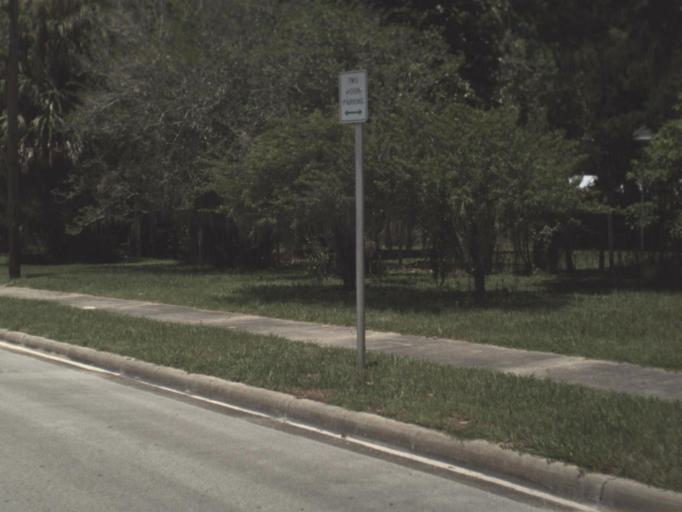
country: US
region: Florida
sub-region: Clay County
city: Keystone Heights
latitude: 29.7098
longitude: -82.0525
